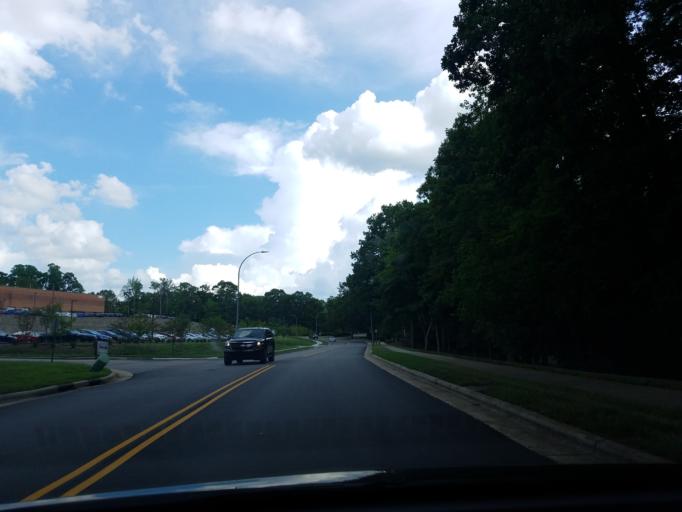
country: US
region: North Carolina
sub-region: Wake County
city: Apex
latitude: 35.7366
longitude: -78.8091
